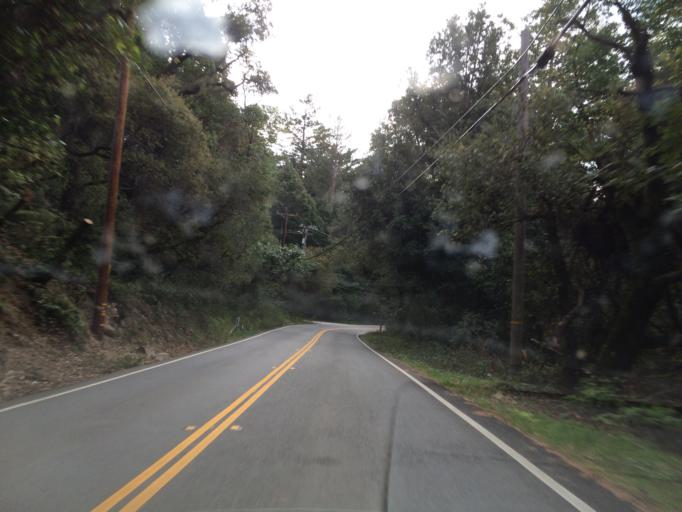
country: US
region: California
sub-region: Santa Cruz County
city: Boulder Creek
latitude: 37.1084
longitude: -122.1456
